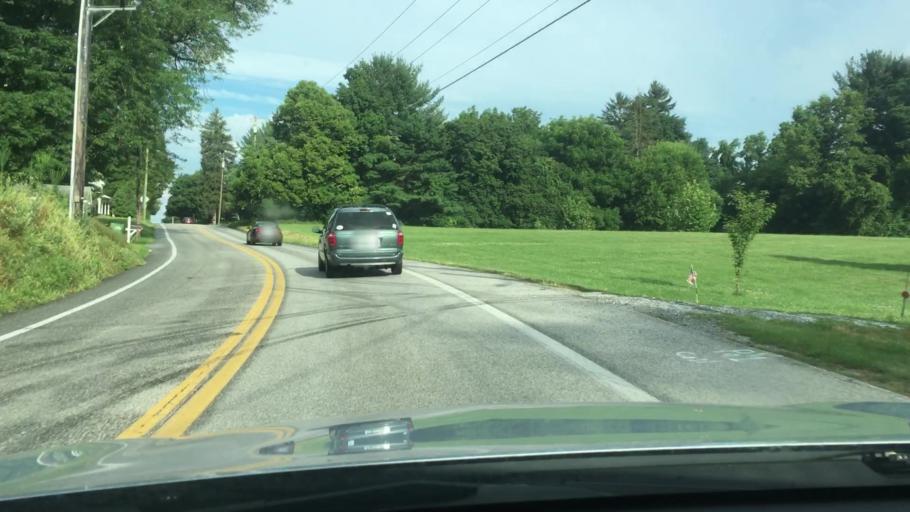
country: US
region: Pennsylvania
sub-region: York County
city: Dillsburg
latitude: 40.1490
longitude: -77.0714
